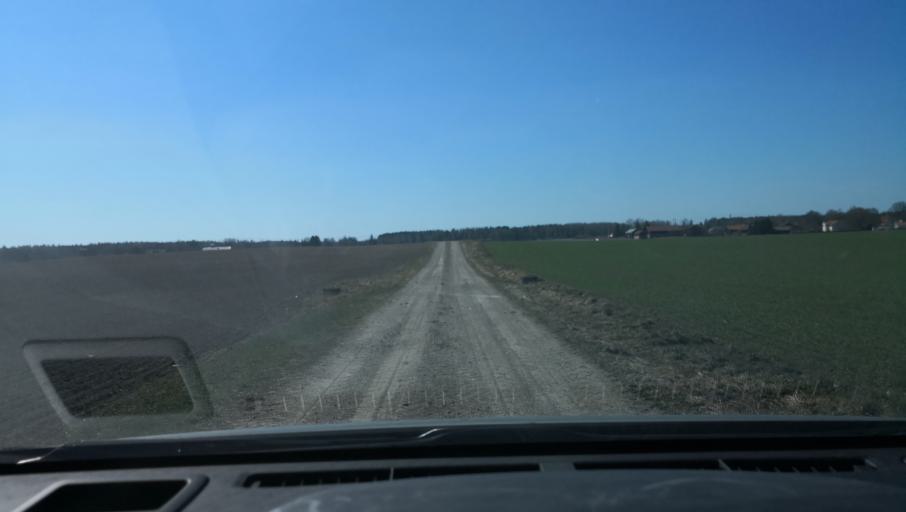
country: SE
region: Vaestmanland
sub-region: Sala Kommun
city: Sala
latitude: 59.8540
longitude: 16.5453
